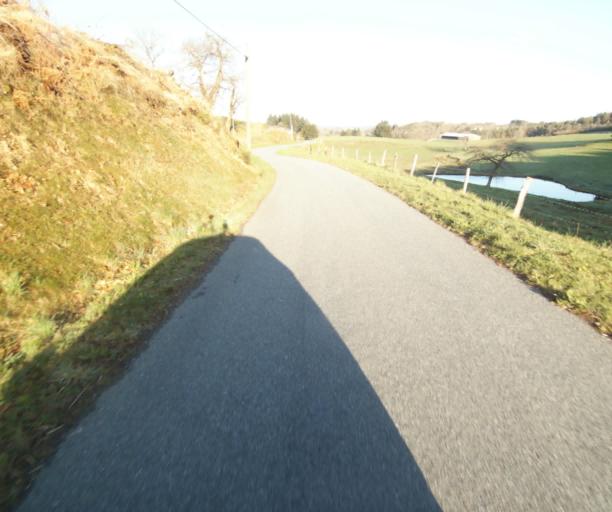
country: FR
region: Limousin
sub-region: Departement de la Correze
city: Correze
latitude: 45.3752
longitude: 1.8609
